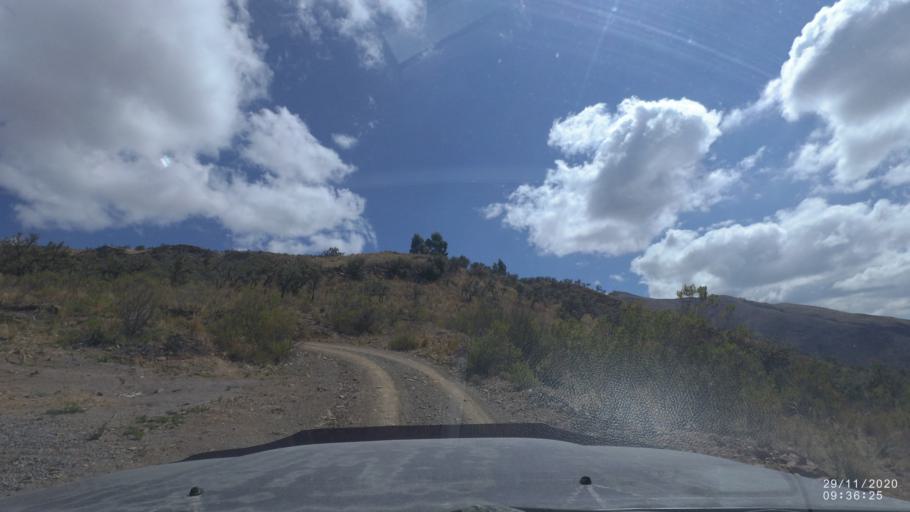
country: BO
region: Cochabamba
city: Cochabamba
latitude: -17.3098
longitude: -66.1874
